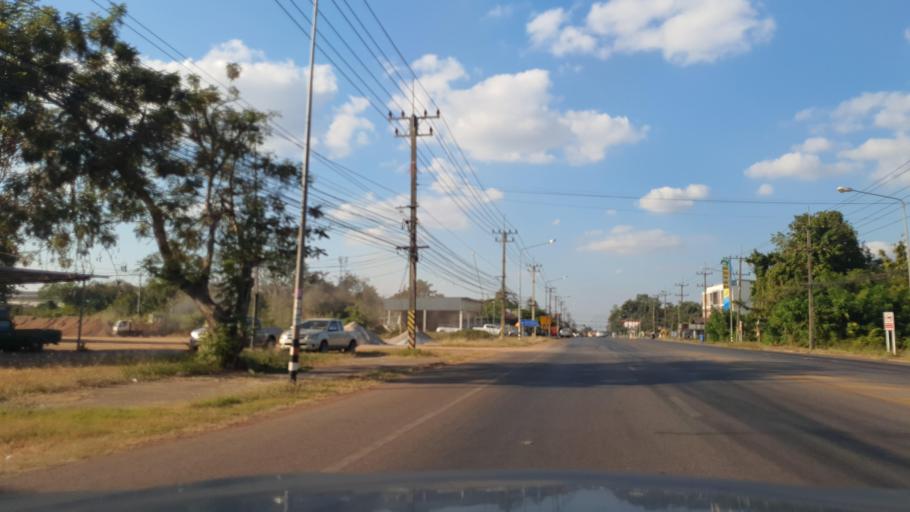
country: TH
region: Sakon Nakhon
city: Sakon Nakhon
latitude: 17.1804
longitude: 104.0952
